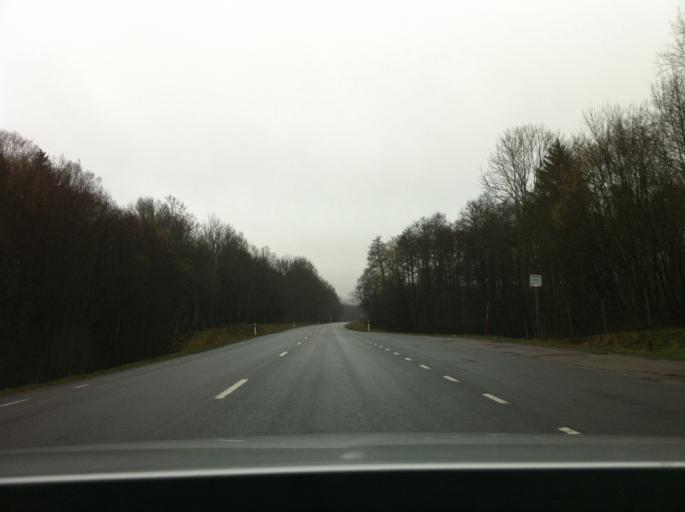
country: SE
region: Vaestra Goetaland
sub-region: Alingsas Kommun
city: Alingsas
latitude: 57.9682
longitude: 12.4445
